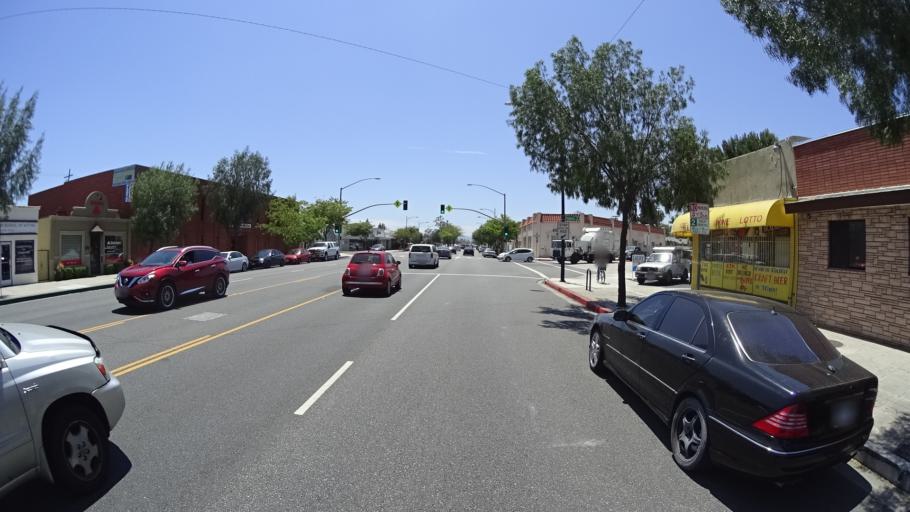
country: US
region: California
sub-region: Los Angeles County
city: Burbank
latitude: 34.1784
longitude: -118.3393
